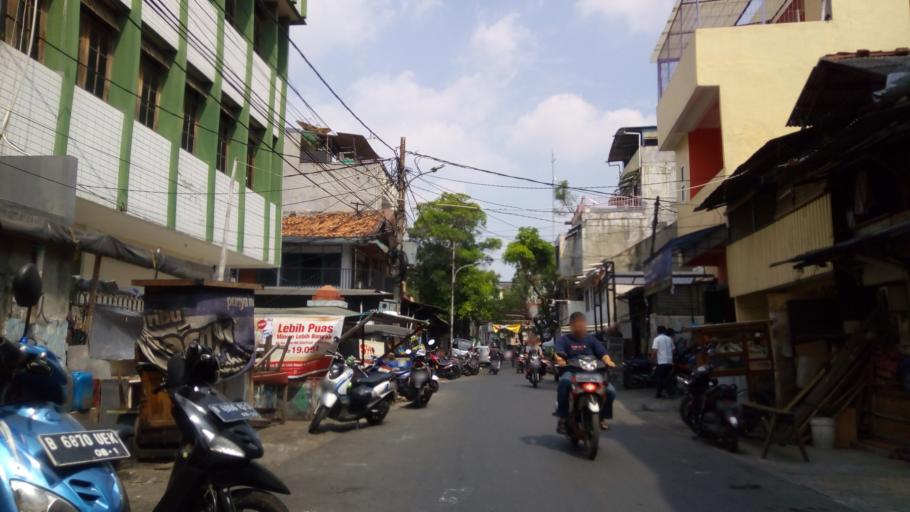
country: ID
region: Jakarta Raya
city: Jakarta
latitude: -6.1574
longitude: 106.8293
